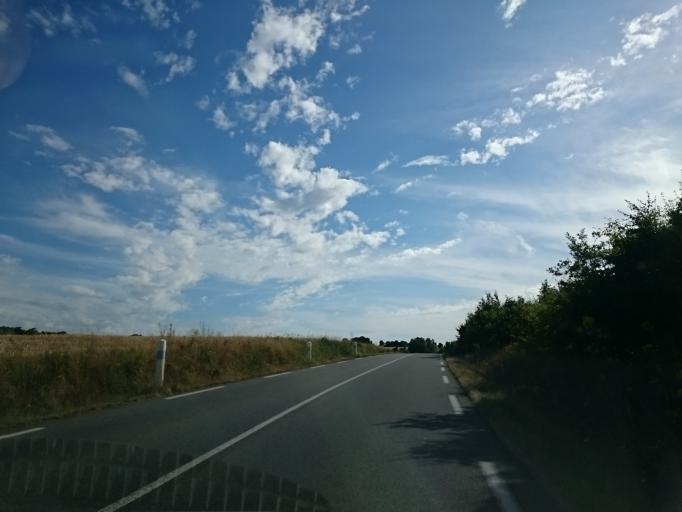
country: FR
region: Brittany
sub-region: Departement d'Ille-et-Vilaine
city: Pance
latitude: 47.8880
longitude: -1.6121
